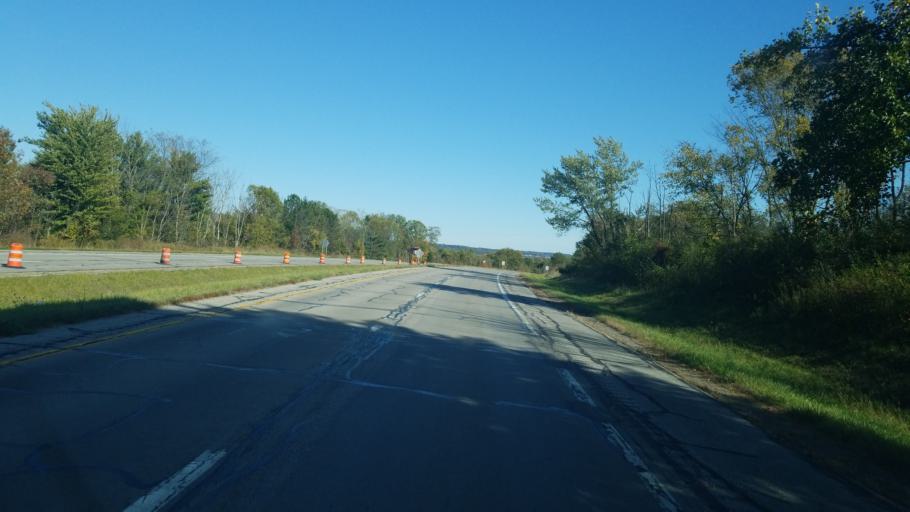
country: US
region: Ohio
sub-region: Medina County
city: Westfield Center
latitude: 41.0391
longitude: -81.9312
